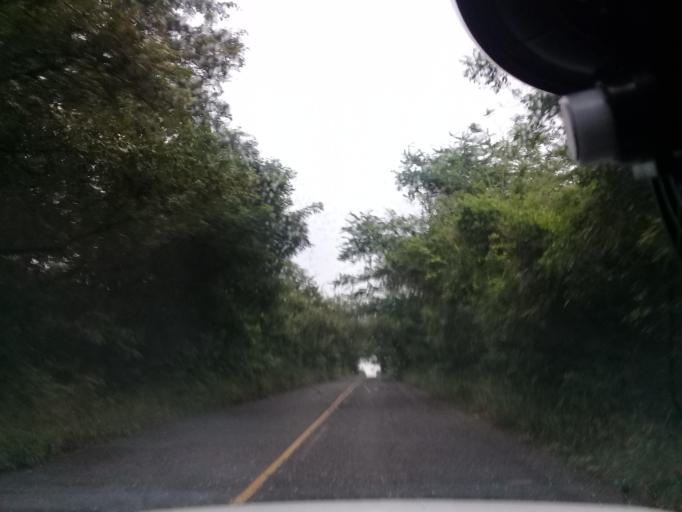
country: MX
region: Veracruz
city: Platon Sanchez
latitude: 21.2275
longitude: -98.3730
